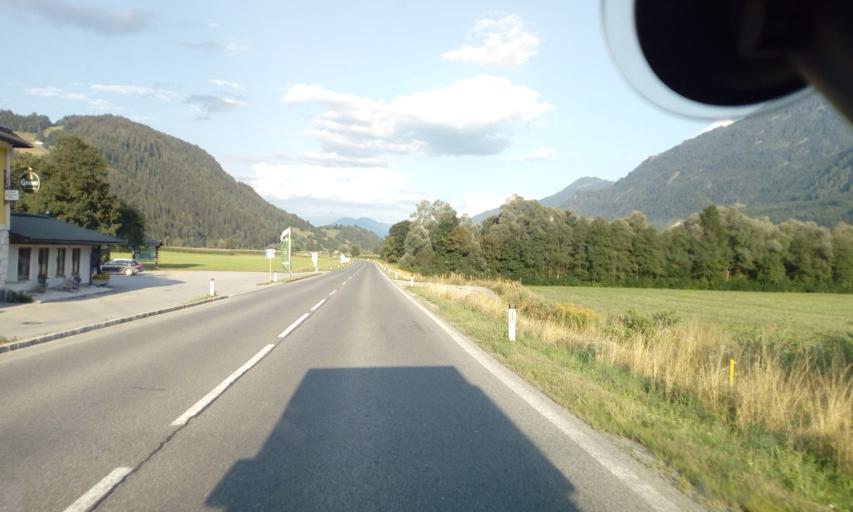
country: AT
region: Carinthia
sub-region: Politischer Bezirk Spittal an der Drau
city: Irschen
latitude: 46.7408
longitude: 13.0317
